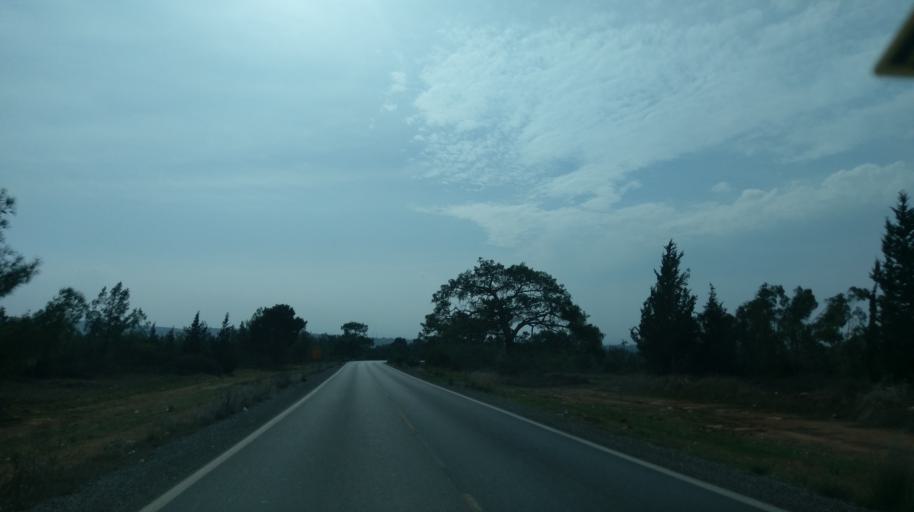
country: CY
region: Lefkosia
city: Morfou
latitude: 35.2750
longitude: 33.0412
